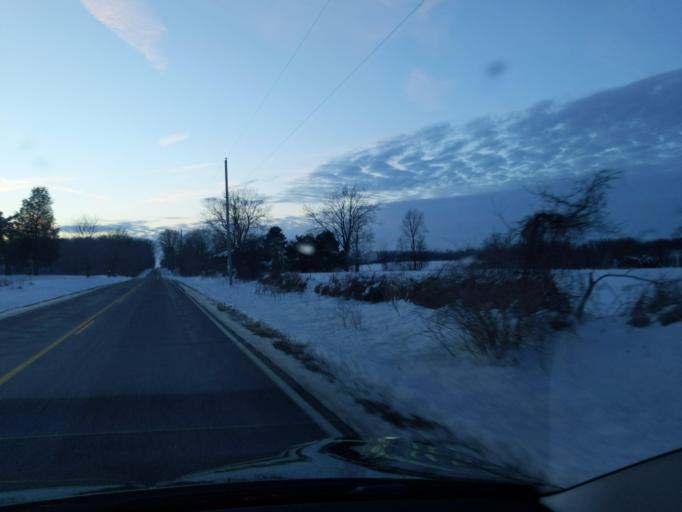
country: US
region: Michigan
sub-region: Ingham County
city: Mason
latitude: 42.5821
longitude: -84.4078
